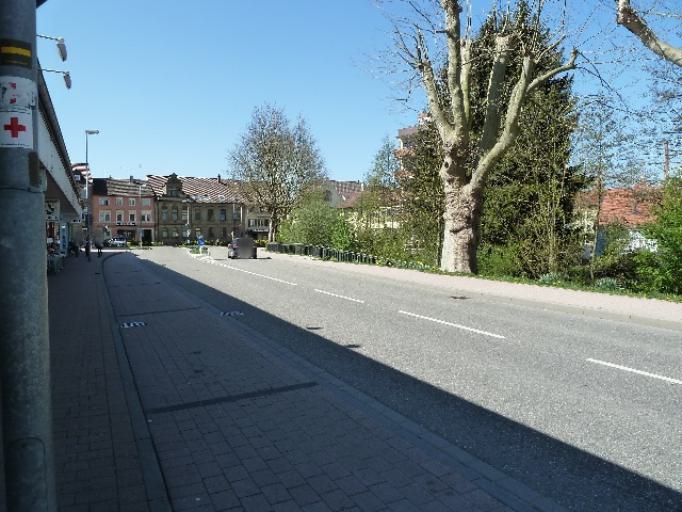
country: DE
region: Baden-Wuerttemberg
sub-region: Regierungsbezirk Stuttgart
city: Eppingen
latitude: 49.1357
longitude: 8.9127
